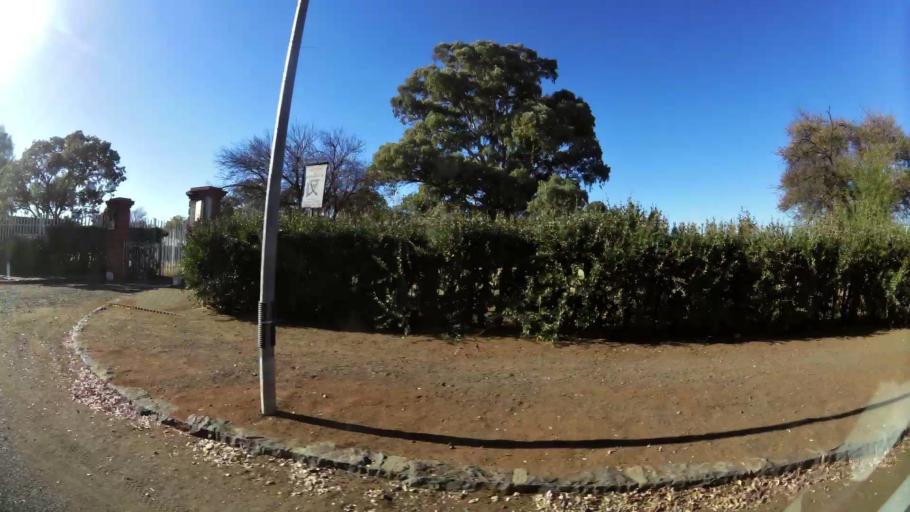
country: ZA
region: Northern Cape
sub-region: Frances Baard District Municipality
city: Kimberley
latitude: -28.7476
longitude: 24.7807
